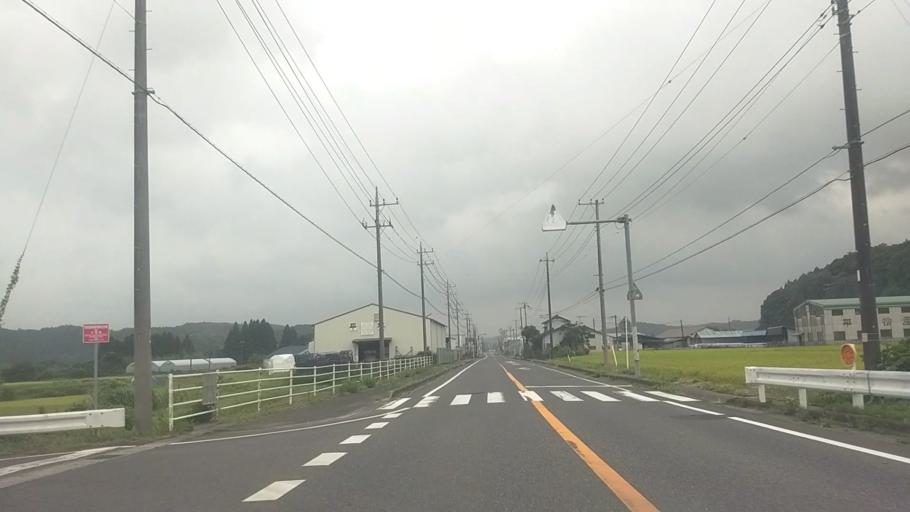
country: JP
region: Chiba
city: Ohara
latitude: 35.2876
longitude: 140.2584
